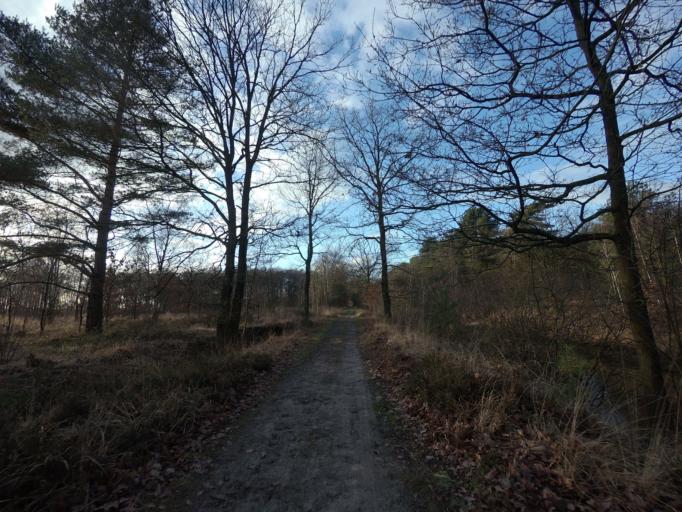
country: BE
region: Flanders
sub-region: Provincie Antwerpen
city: Kapellen
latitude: 51.3470
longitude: 4.4219
